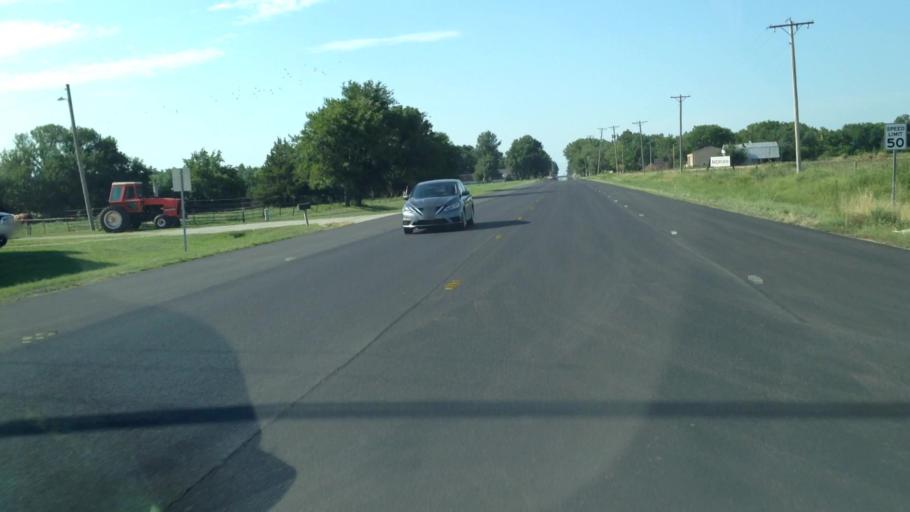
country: US
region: Kansas
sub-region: Allen County
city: Iola
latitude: 37.9072
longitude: -95.1702
